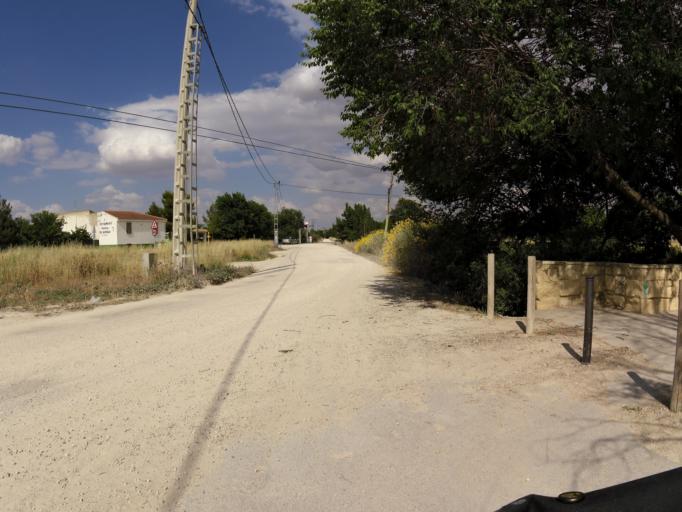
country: ES
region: Castille-La Mancha
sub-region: Provincia de Albacete
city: Albacete
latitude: 38.9968
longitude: -1.8916
